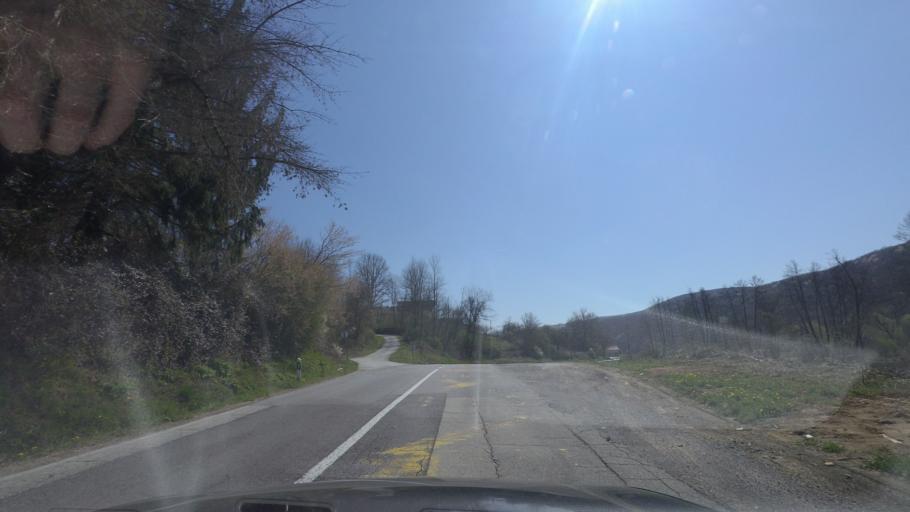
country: HR
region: Karlovacka
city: Vojnic
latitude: 45.3751
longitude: 15.6515
